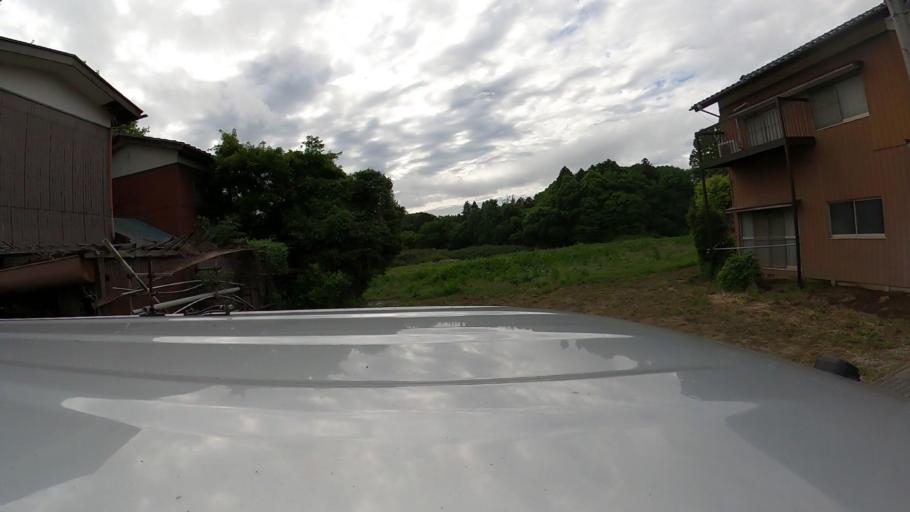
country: JP
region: Ibaraki
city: Ami
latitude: 35.9662
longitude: 140.2295
